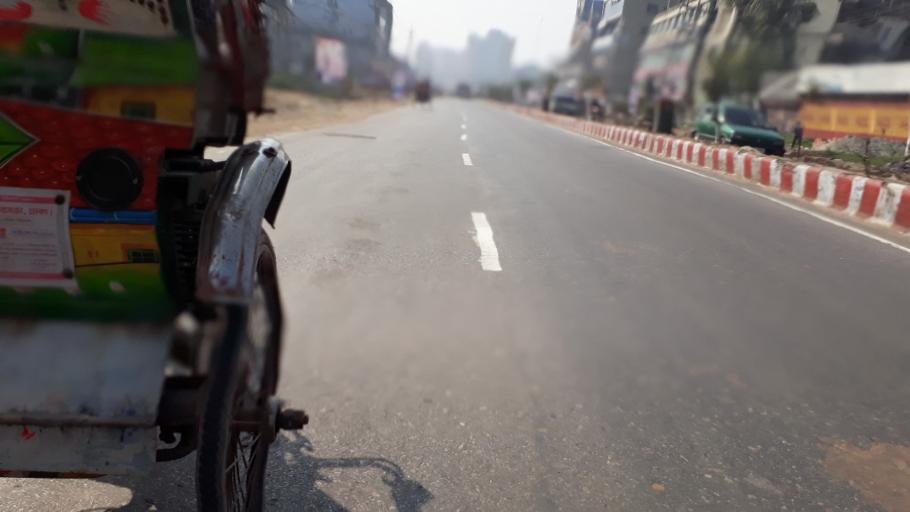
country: BD
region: Dhaka
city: Tungi
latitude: 23.8562
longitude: 90.2612
